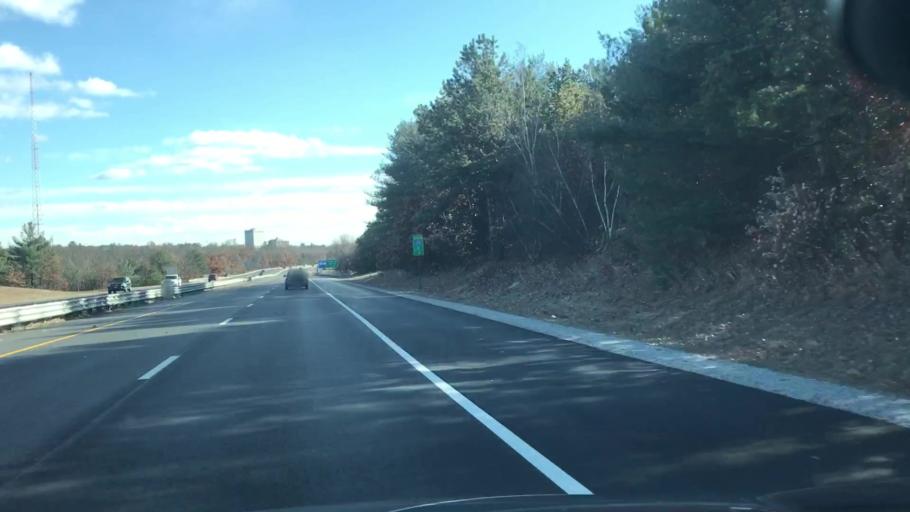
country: US
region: New Hampshire
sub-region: Hillsborough County
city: Pinardville
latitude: 43.0170
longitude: -71.4834
